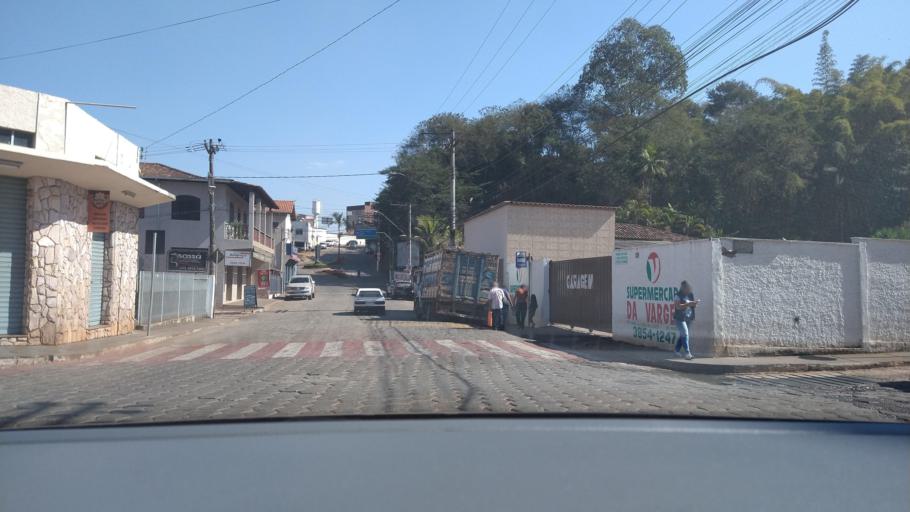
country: BR
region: Minas Gerais
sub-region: Rio Piracicaba
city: Rio Piracicaba
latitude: -19.9278
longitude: -43.1692
